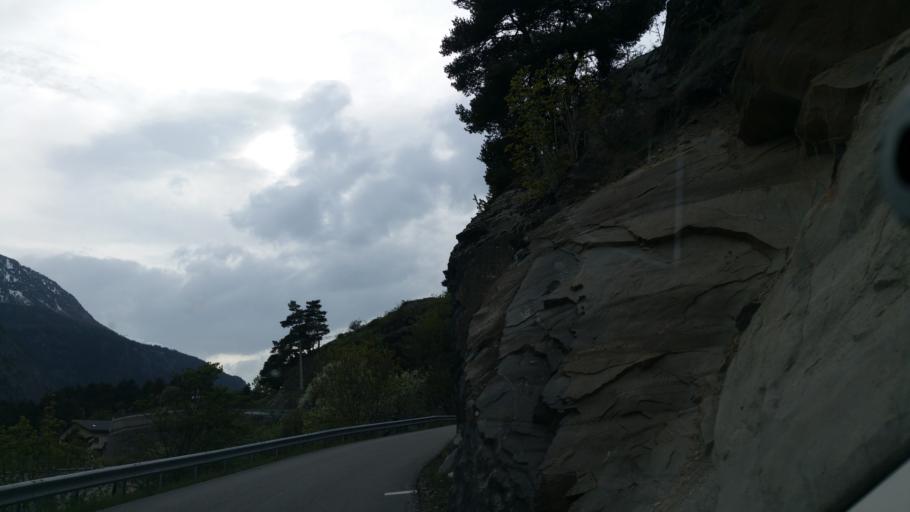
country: FR
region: Rhone-Alpes
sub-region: Departement de la Savoie
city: Modane
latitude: 45.2022
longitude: 6.6183
